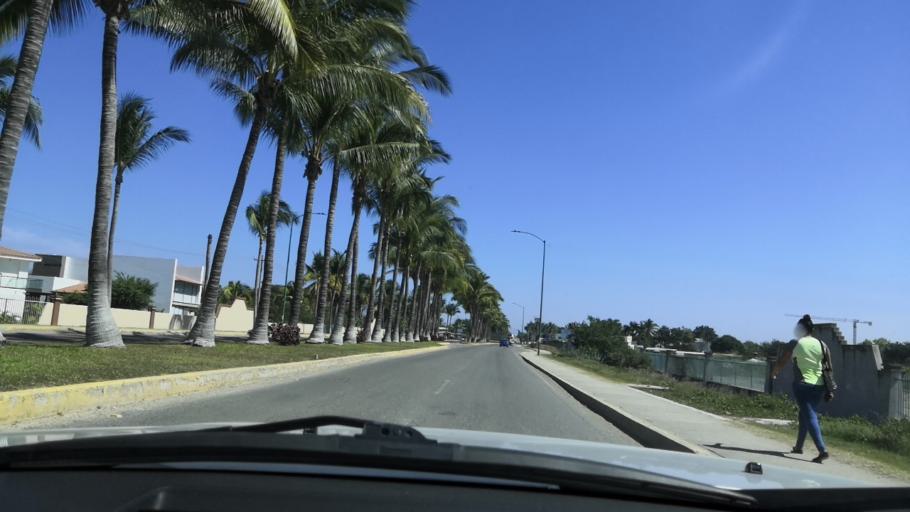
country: MX
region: Nayarit
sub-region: Bahia de Banderas
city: Las Jarretaderas
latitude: 20.6972
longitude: -105.2781
